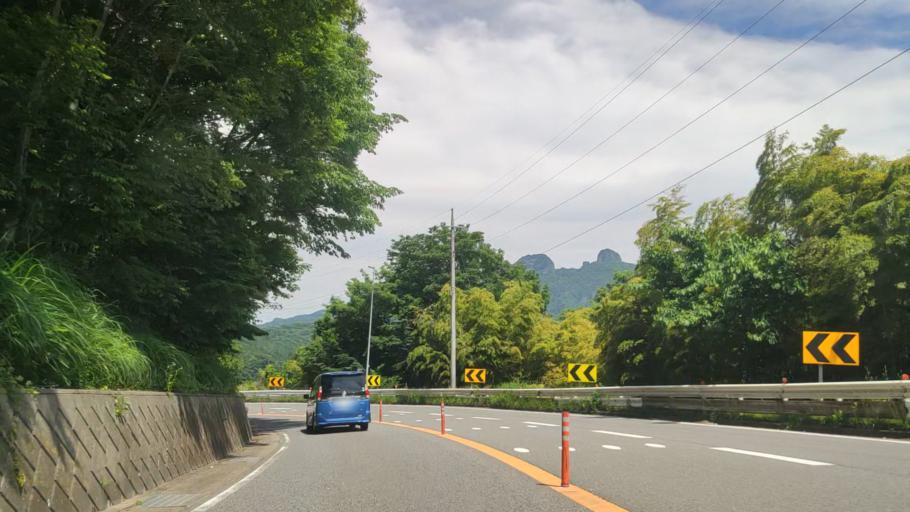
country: JP
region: Gunma
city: Annaka
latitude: 36.3296
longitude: 138.6762
